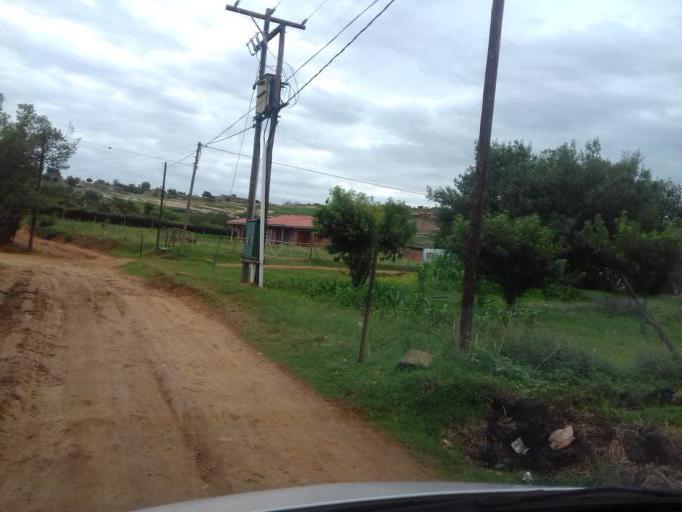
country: LS
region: Berea
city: Teyateyaneng
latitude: -29.1172
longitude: 27.9659
